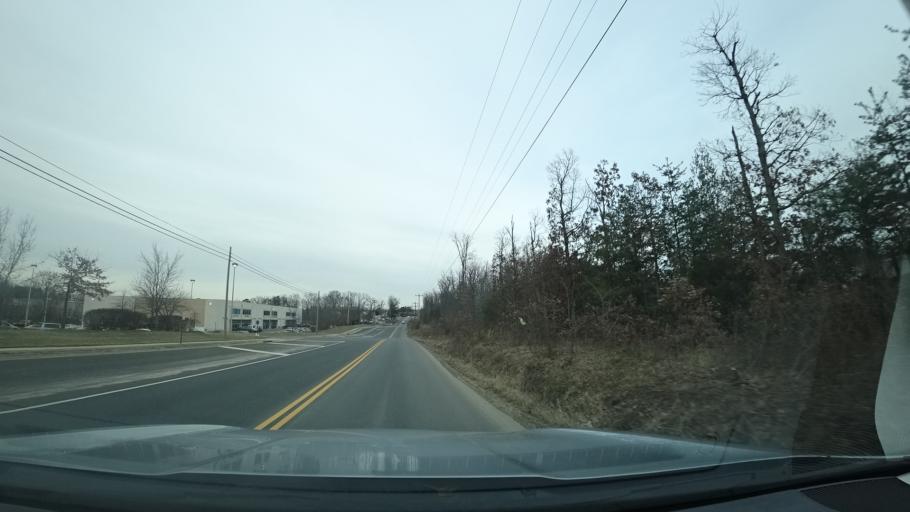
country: US
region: Virginia
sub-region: Loudoun County
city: Oak Grove
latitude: 38.9732
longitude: -77.4118
